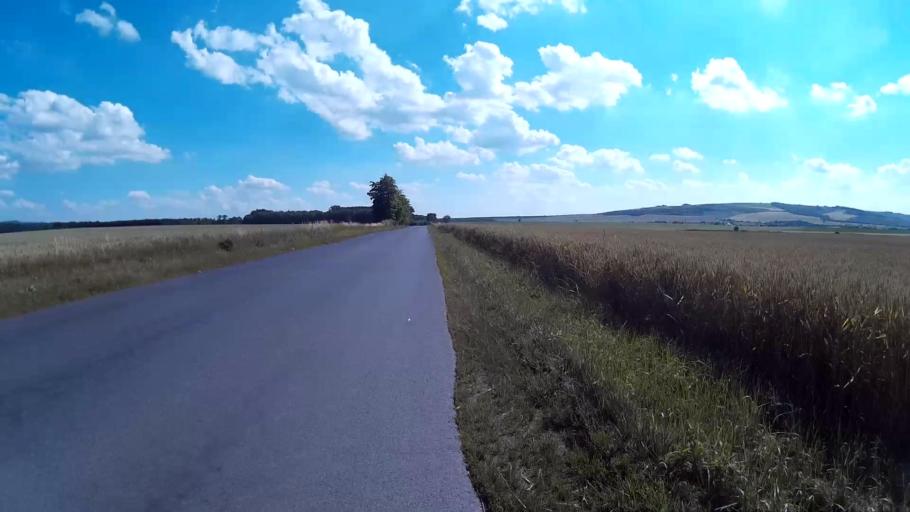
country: CZ
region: South Moravian
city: Menin
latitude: 49.0527
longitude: 16.7030
